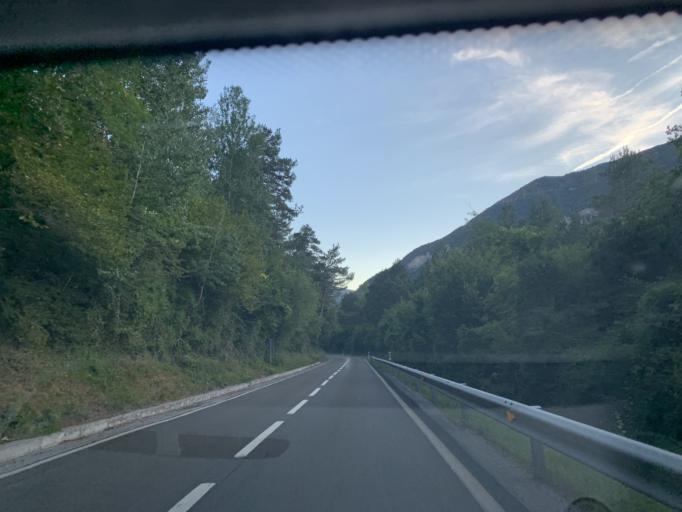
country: ES
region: Aragon
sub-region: Provincia de Huesca
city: Broto
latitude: 42.5659
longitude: -0.1134
